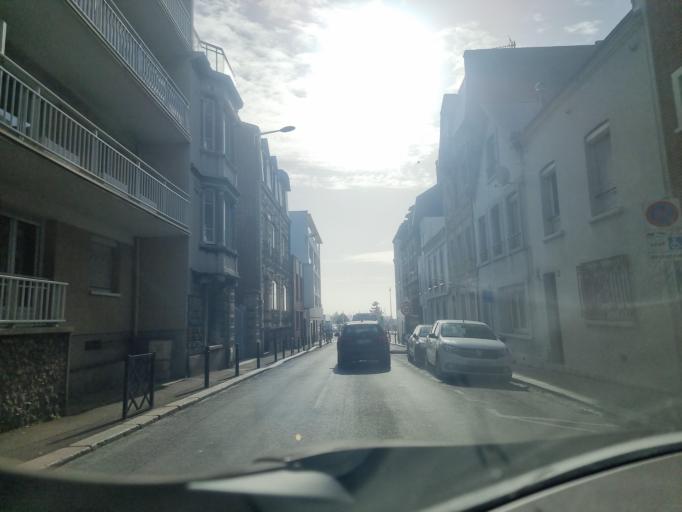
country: FR
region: Haute-Normandie
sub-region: Departement de la Seine-Maritime
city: Le Havre
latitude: 49.4965
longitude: 0.0941
